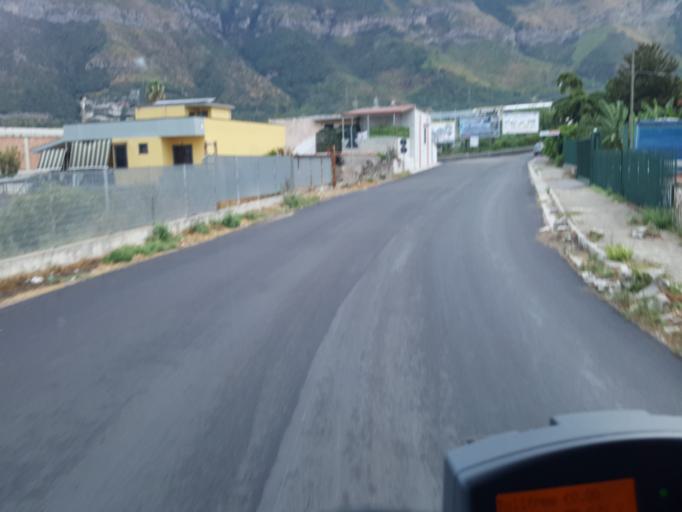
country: IT
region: Campania
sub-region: Provincia di Napoli
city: Striano
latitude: 40.8232
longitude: 14.5981
